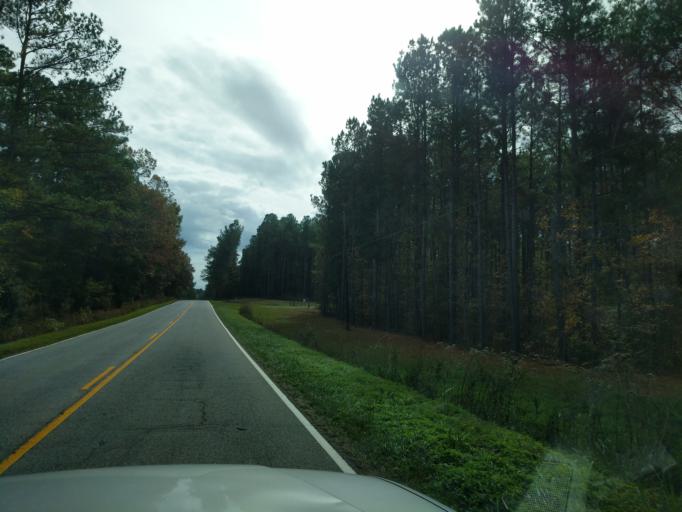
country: US
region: South Carolina
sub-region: Saluda County
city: Saluda
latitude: 34.0900
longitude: -81.8272
